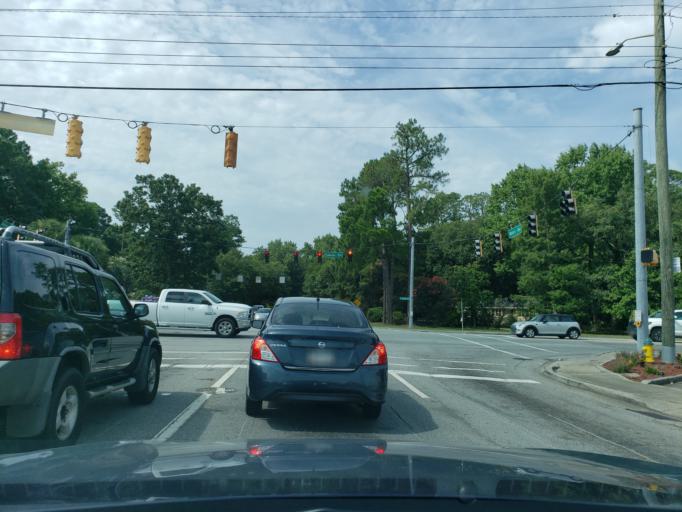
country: US
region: Georgia
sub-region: Chatham County
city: Thunderbolt
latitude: 32.0247
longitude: -81.0946
